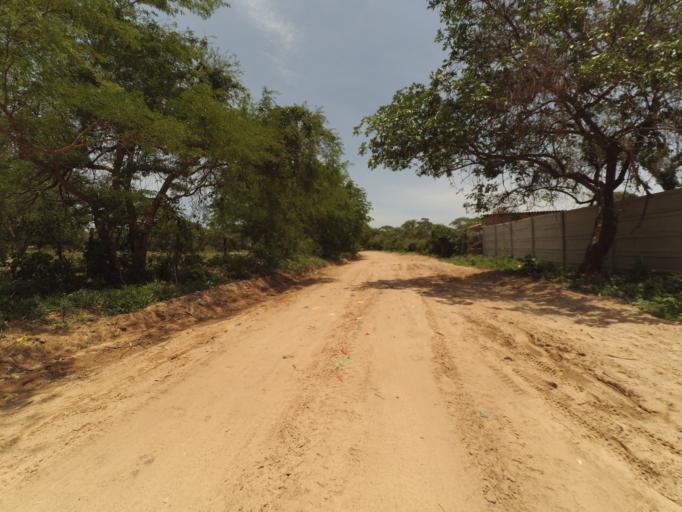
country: BO
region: Santa Cruz
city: Santa Cruz de la Sierra
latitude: -17.8184
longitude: -63.2559
